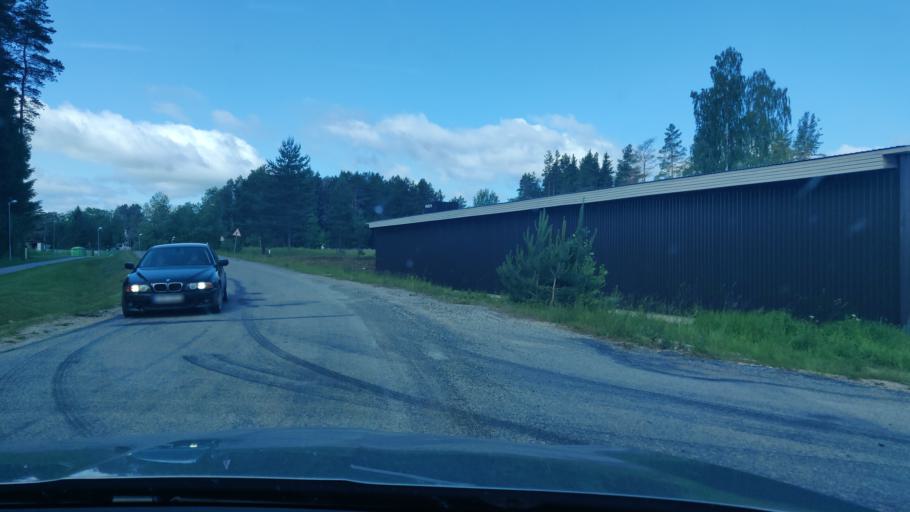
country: EE
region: Vorumaa
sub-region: Voru linn
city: Voru
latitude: 57.7312
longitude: 27.2729
